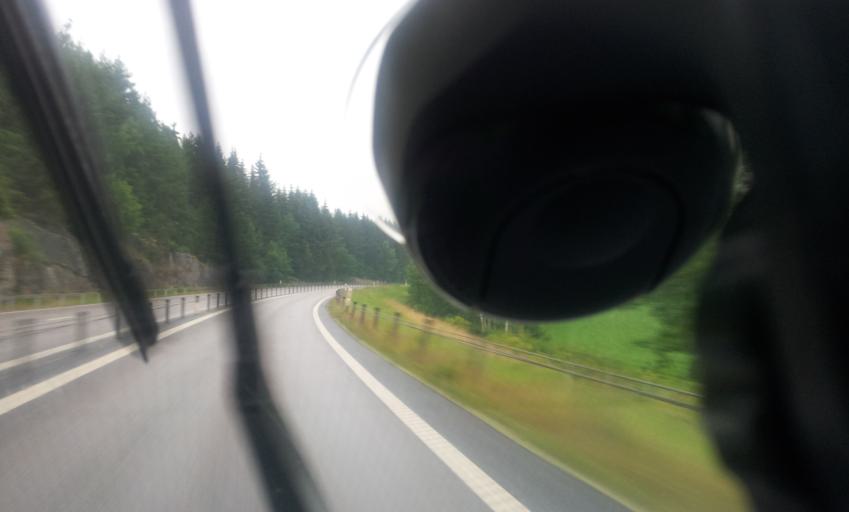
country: SE
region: Kalmar
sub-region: Vasterviks Kommun
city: Gamleby
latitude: 57.9267
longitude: 16.3977
